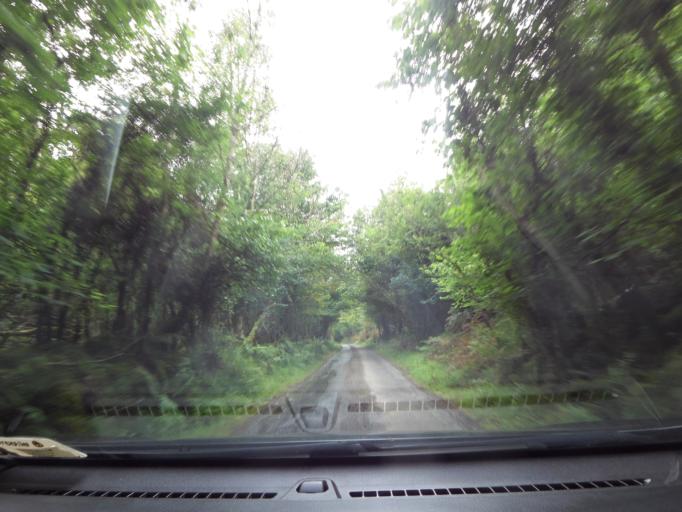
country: IE
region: Connaught
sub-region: County Galway
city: Loughrea
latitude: 53.1360
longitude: -8.4756
